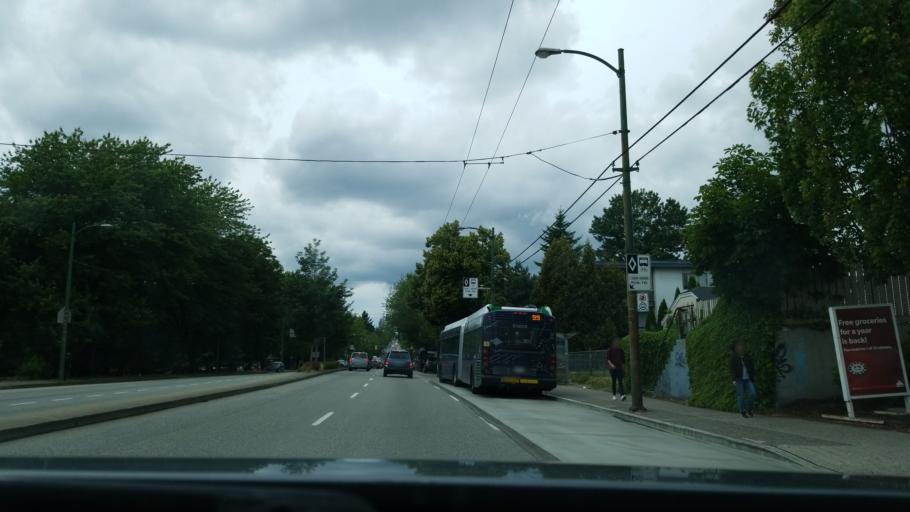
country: CA
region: British Columbia
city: Vancouver
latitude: 49.2624
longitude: -123.0780
